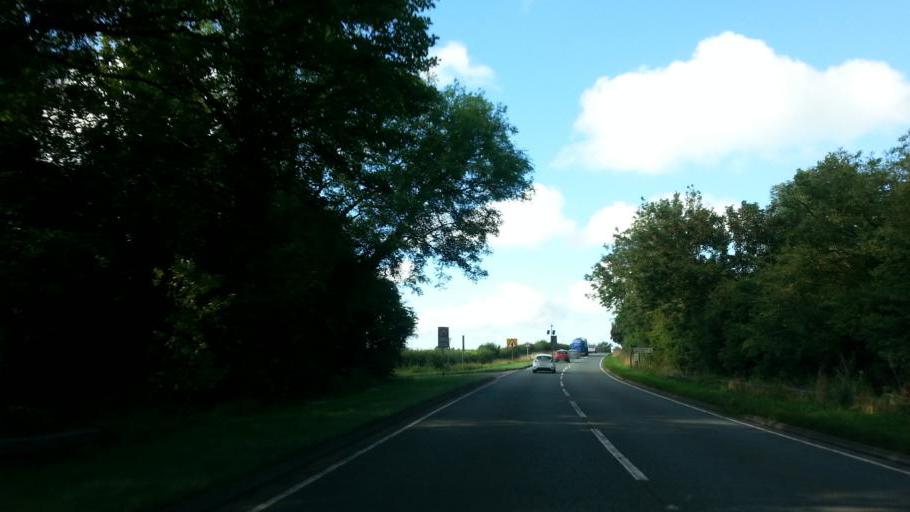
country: GB
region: England
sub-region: District of Rutland
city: Morcott
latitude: 52.5188
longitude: -0.5932
